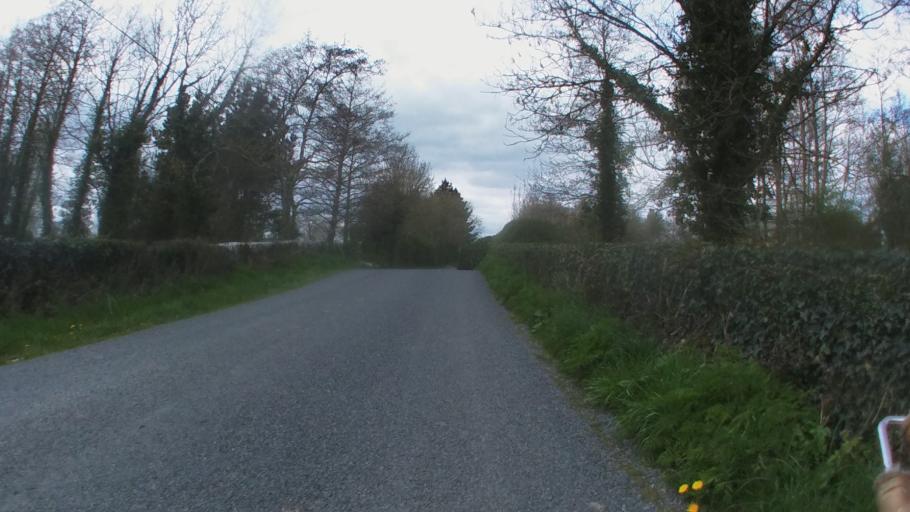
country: IE
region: Leinster
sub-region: Kilkenny
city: Kilkenny
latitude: 52.6558
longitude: -7.1831
